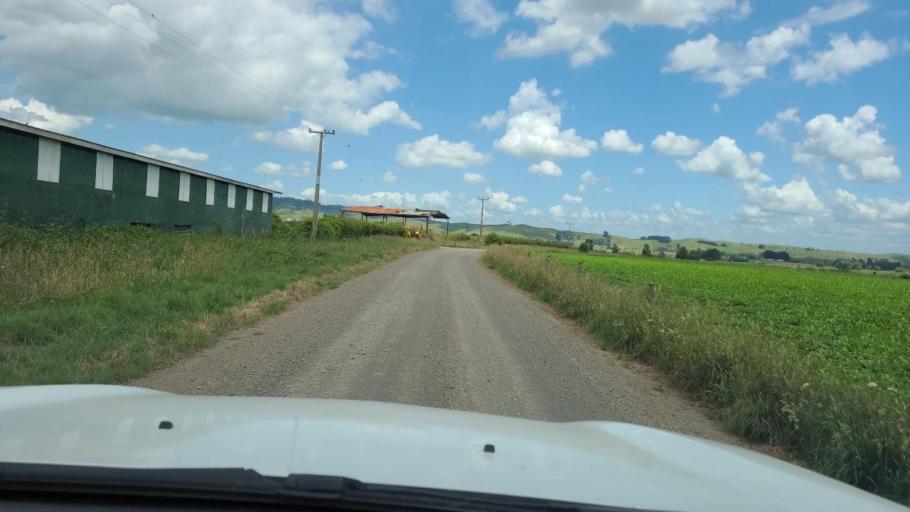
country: NZ
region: Waikato
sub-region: Hauraki District
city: Ngatea
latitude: -37.5192
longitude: 175.4119
